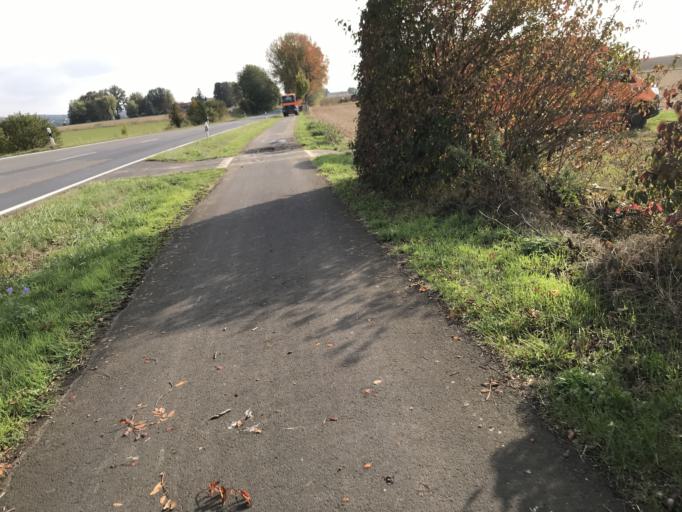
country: DE
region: Hesse
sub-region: Regierungsbezirk Giessen
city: Langgons
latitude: 50.5156
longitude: 8.6524
